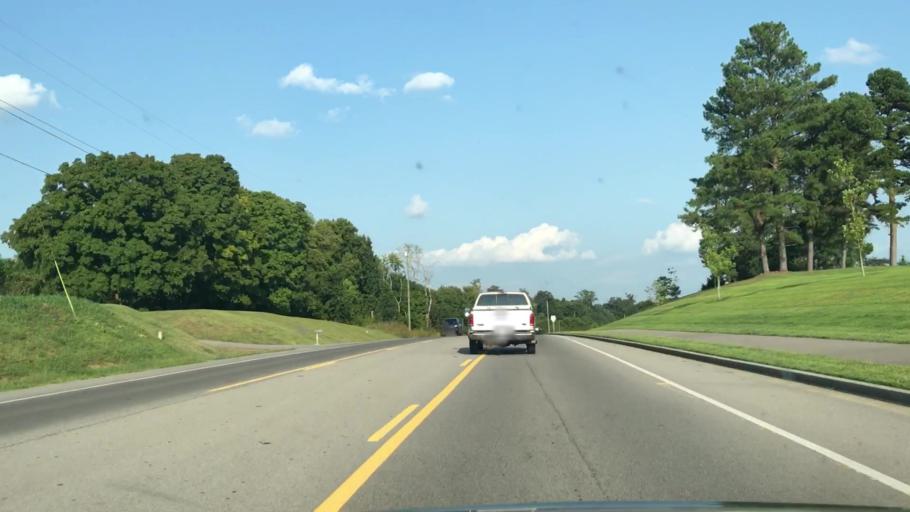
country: US
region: Tennessee
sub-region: Williamson County
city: Brentwood Estates
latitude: 35.9899
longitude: -86.7443
